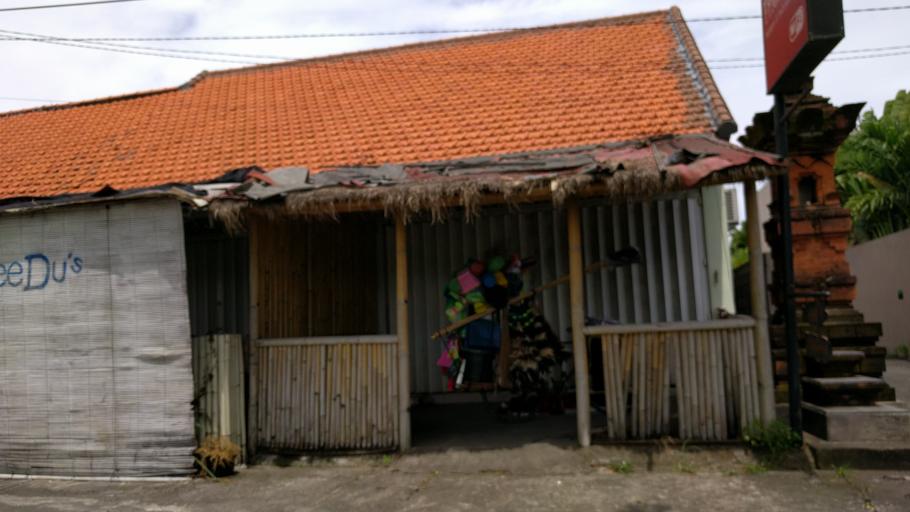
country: ID
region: Bali
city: Banjar Gunungpande
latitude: -8.6526
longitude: 115.1488
